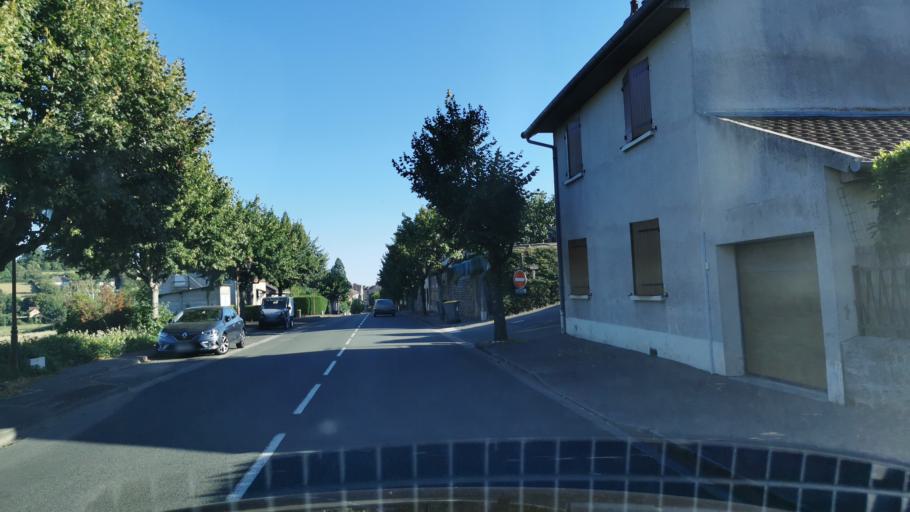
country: FR
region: Bourgogne
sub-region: Departement de Saone-et-Loire
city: Montcenis
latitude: 46.7960
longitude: 4.3893
